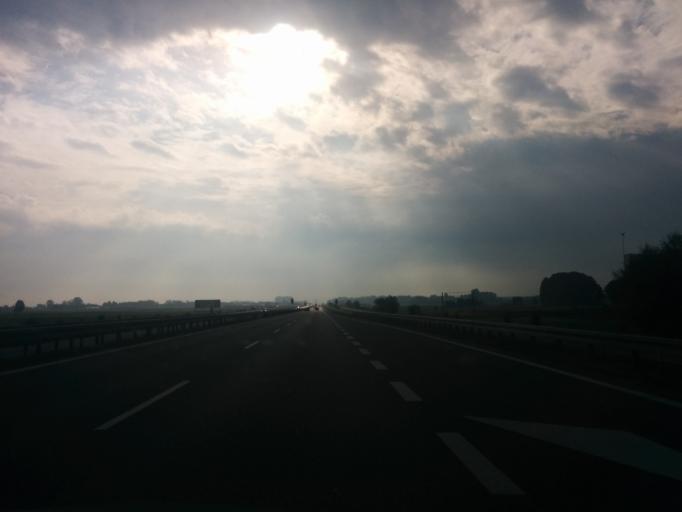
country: PL
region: Masovian Voivodeship
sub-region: Powiat radomski
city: Jedlinsk
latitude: 51.5399
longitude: 21.0650
